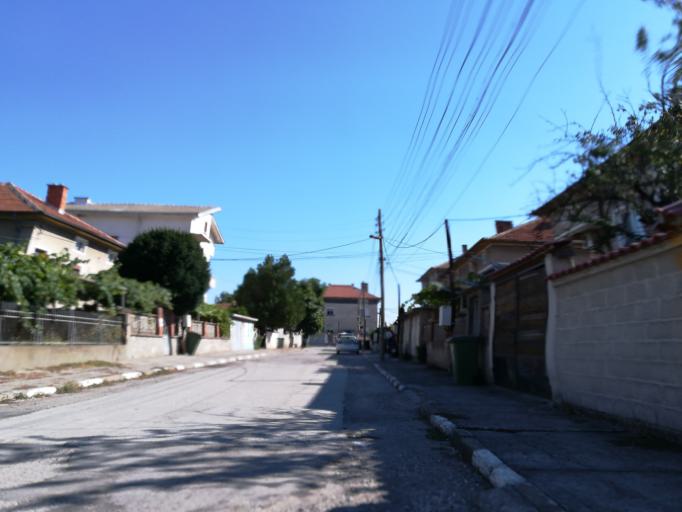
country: BG
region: Stara Zagora
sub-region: Obshtina Chirpan
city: Chirpan
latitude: 42.0943
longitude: 25.2222
